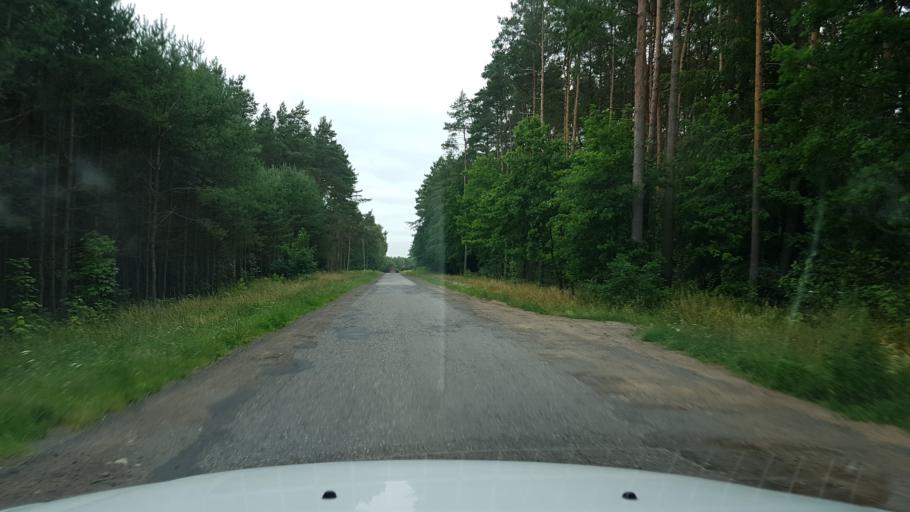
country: PL
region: West Pomeranian Voivodeship
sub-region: Powiat gryficki
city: Brojce
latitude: 53.9456
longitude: 15.3918
